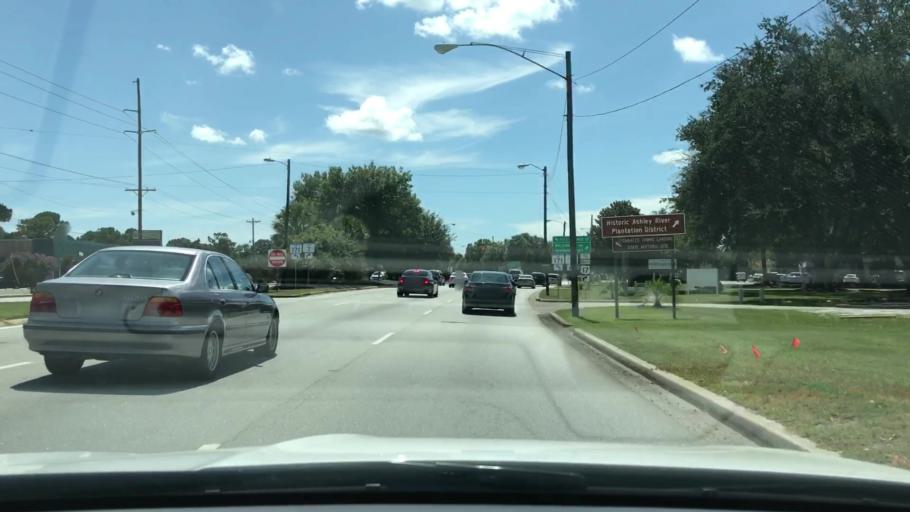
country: US
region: South Carolina
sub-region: Charleston County
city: North Charleston
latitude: 32.8191
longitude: -79.9929
